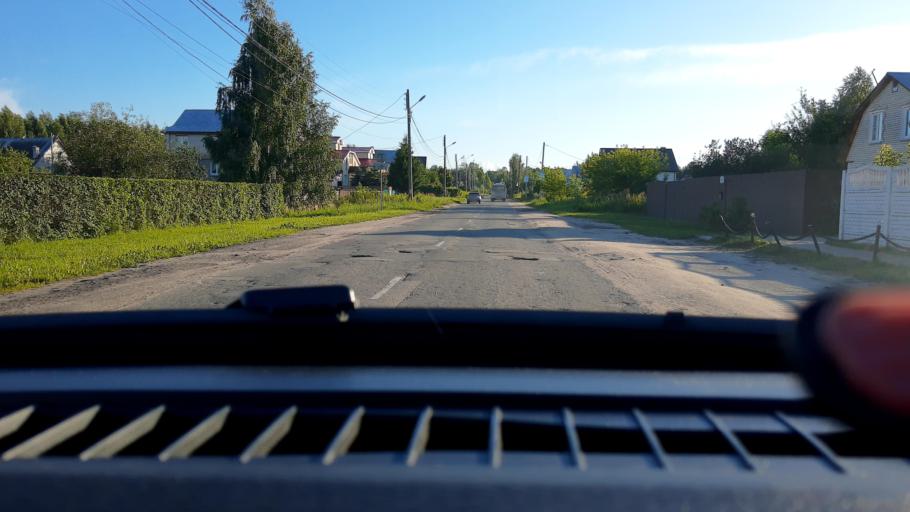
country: RU
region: Nizjnij Novgorod
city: Bor
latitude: 56.3372
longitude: 44.1349
